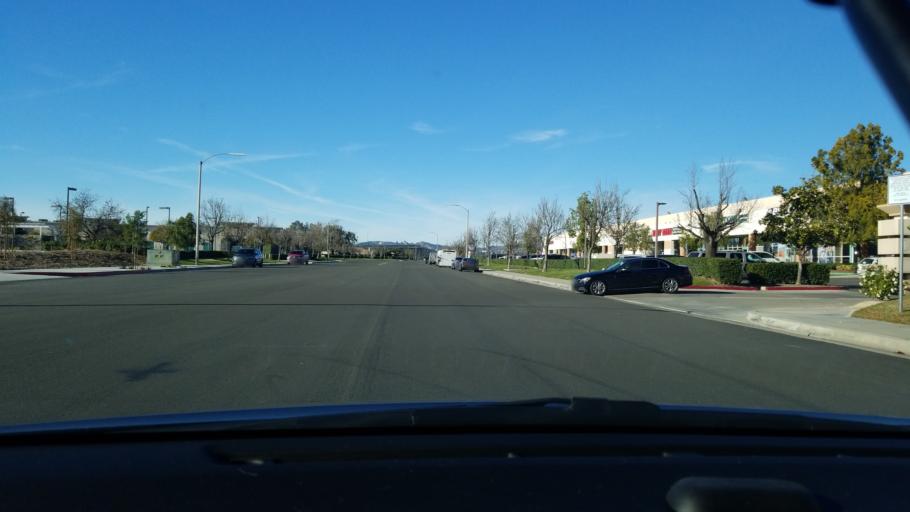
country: US
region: California
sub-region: Riverside County
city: Murrieta Hot Springs
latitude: 33.5257
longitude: -117.1670
